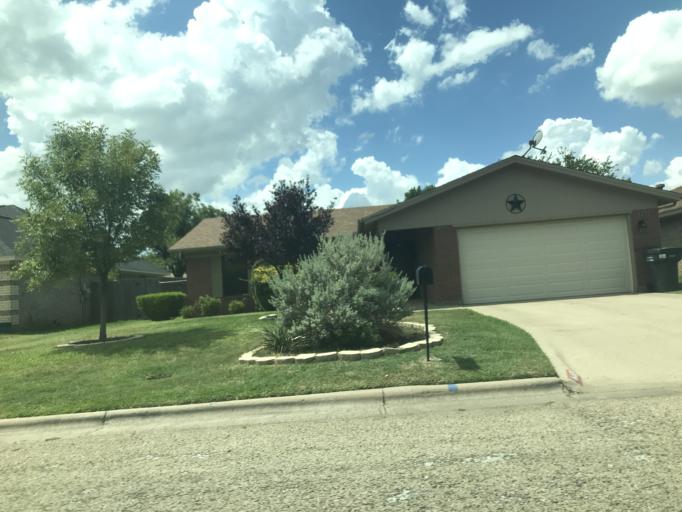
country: US
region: Texas
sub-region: Taylor County
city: Abilene
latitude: 32.4414
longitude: -99.6998
